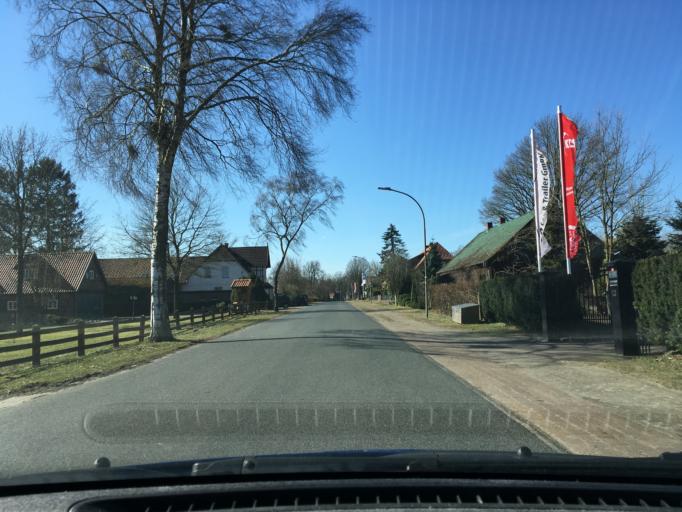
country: DE
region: Lower Saxony
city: Neuenkirchen
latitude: 53.0687
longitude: 9.6730
